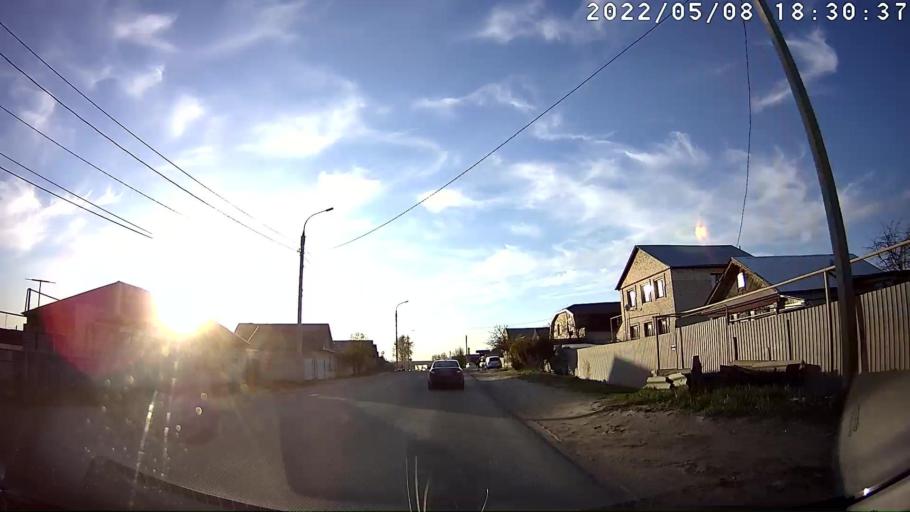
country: RU
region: Mariy-El
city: Volzhsk
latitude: 55.8746
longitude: 48.3628
